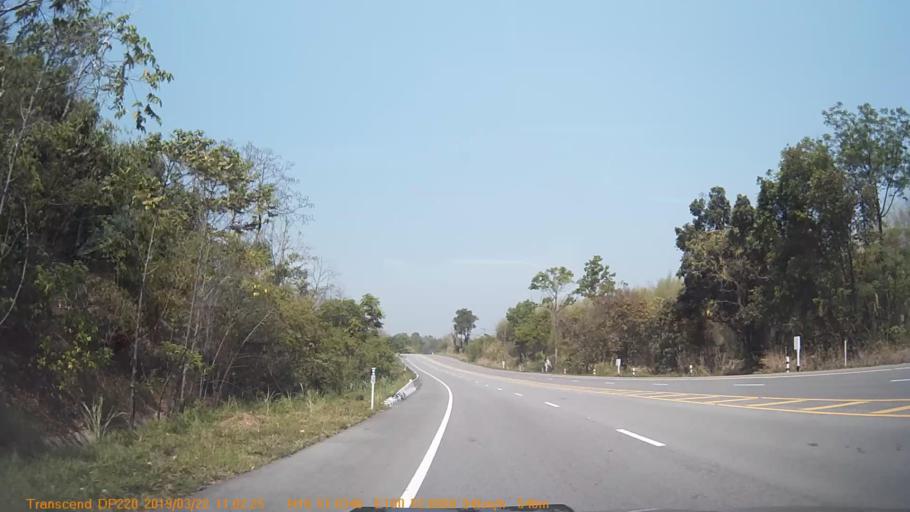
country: TH
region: Phetchabun
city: Khao Kho
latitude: 16.8508
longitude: 100.8778
